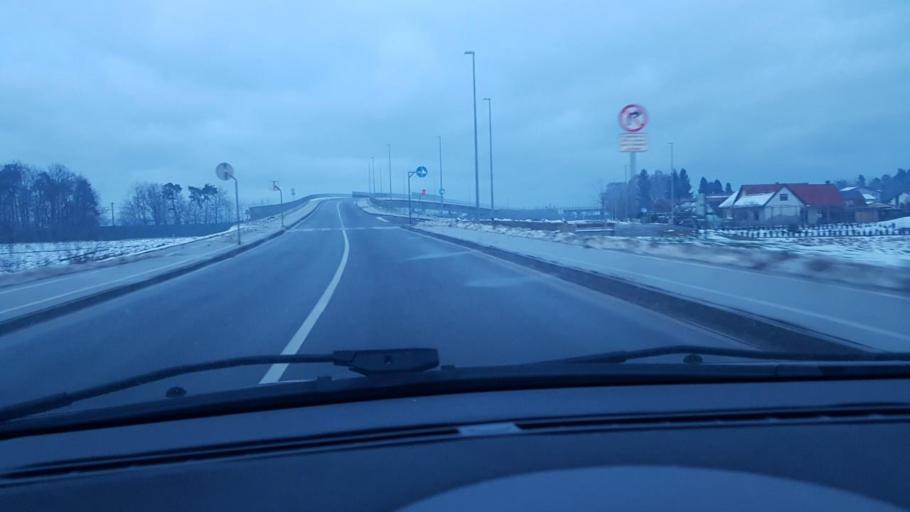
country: SI
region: Hajdina
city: Spodnja Hajdina
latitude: 46.3989
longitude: 15.8255
